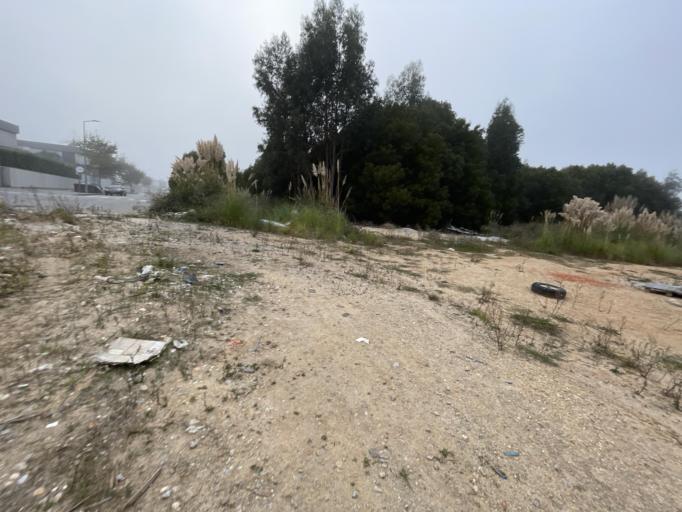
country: PT
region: Porto
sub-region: Vila Nova de Gaia
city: Canidelo
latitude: 41.1046
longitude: -8.6566
